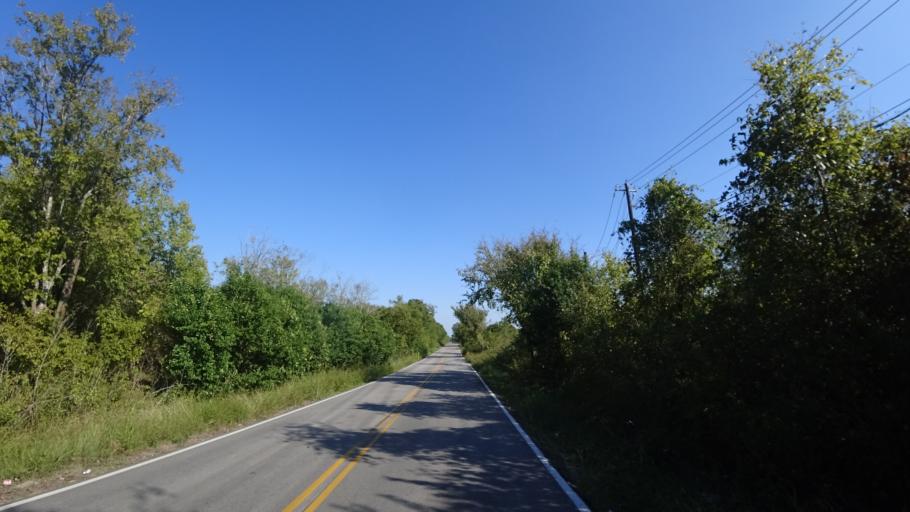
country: US
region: Texas
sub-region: Travis County
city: Manor
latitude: 30.3412
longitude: -97.6617
